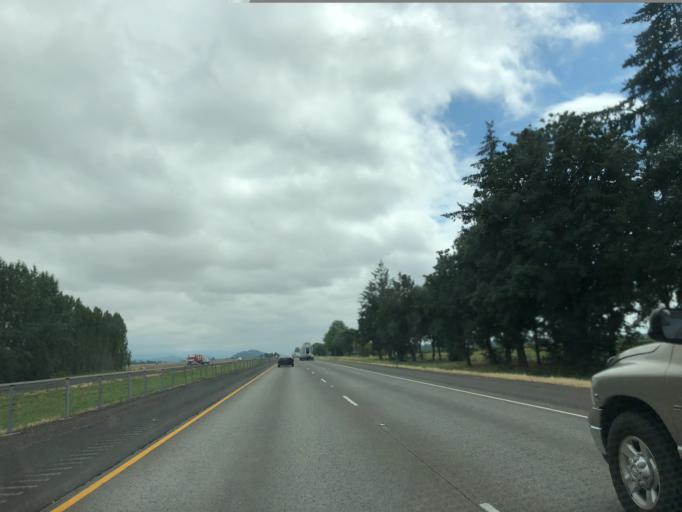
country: US
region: Oregon
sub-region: Linn County
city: Tangent
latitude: 44.5290
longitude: -123.0620
